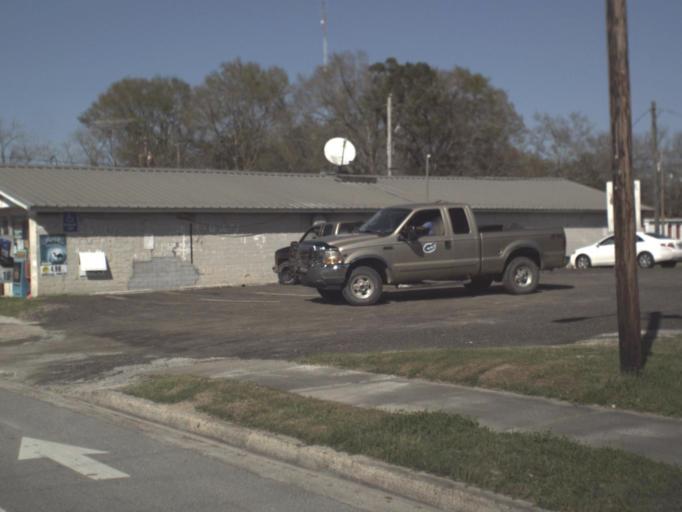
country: US
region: Florida
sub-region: Gulf County
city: Wewahitchka
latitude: 30.1128
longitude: -85.2002
